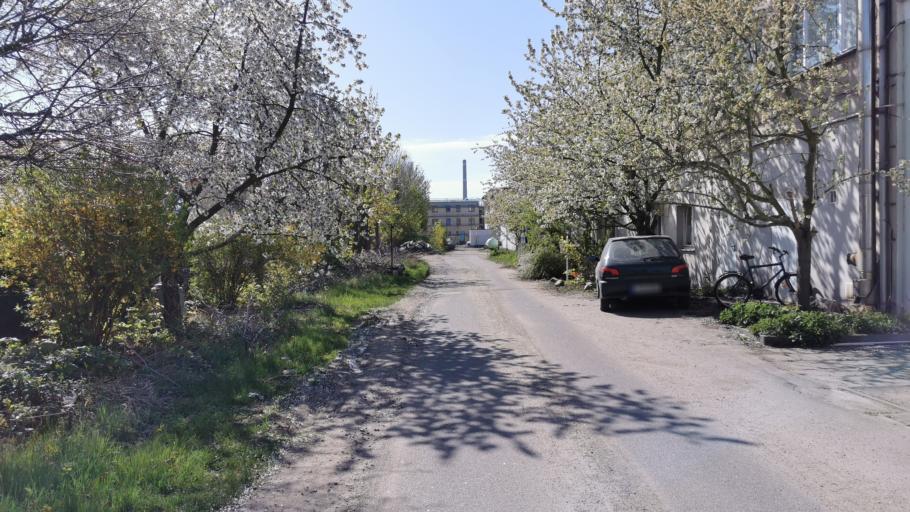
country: DE
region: Saxony
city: Markranstadt
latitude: 51.3065
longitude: 12.2302
